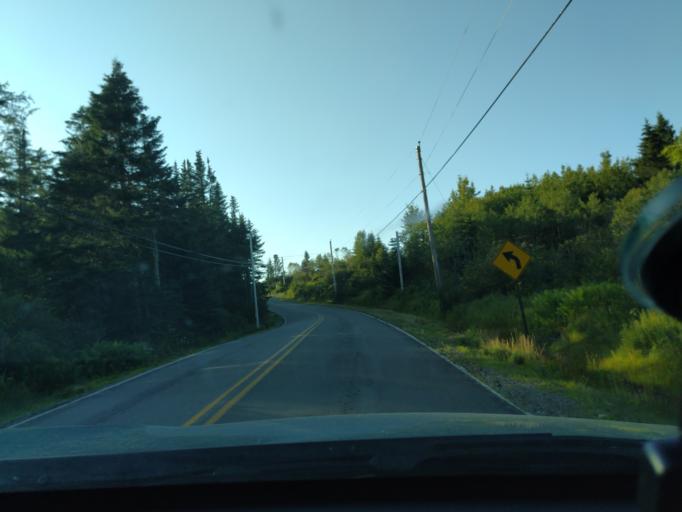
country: US
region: Maine
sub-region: Washington County
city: Machiasport
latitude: 44.6673
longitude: -67.2389
